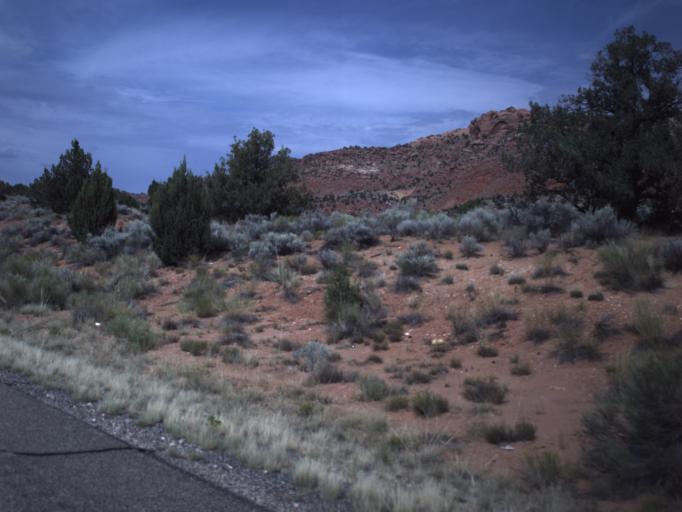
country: US
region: Utah
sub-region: Kane County
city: Kanab
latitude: 37.1601
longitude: -111.9695
